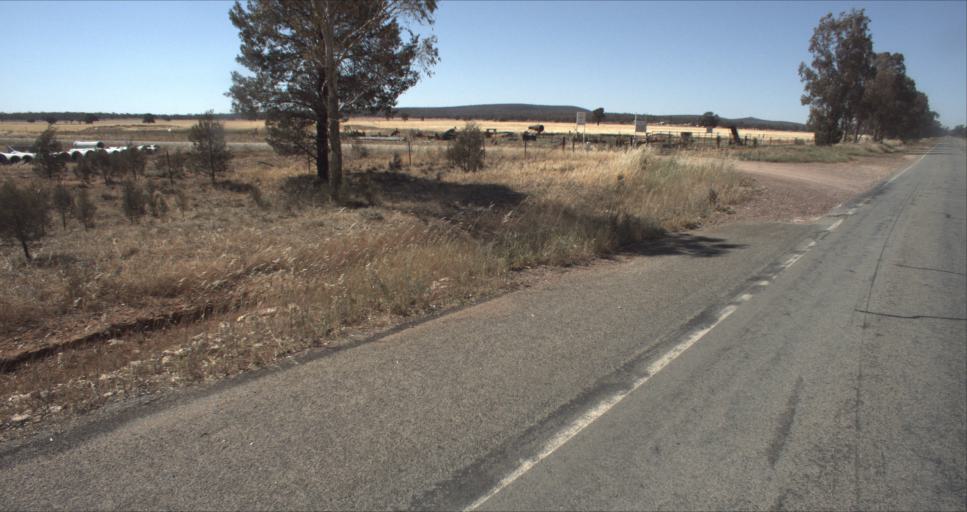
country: AU
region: New South Wales
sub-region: Leeton
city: Leeton
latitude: -34.4983
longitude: 146.4523
